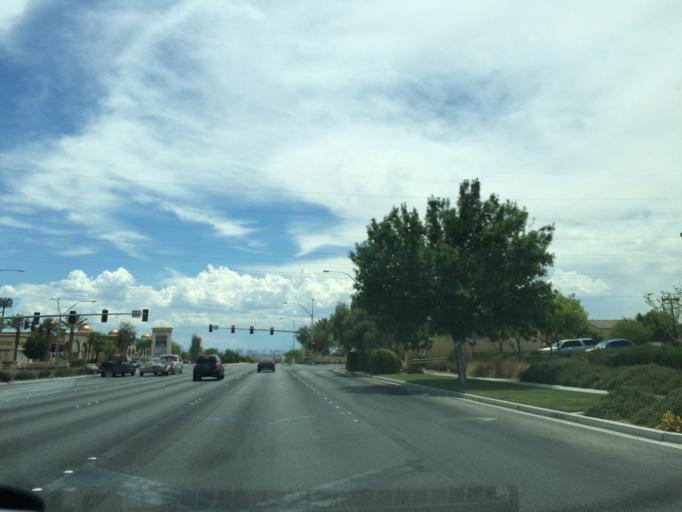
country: US
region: Nevada
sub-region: Clark County
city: North Las Vegas
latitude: 36.2773
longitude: -115.1799
